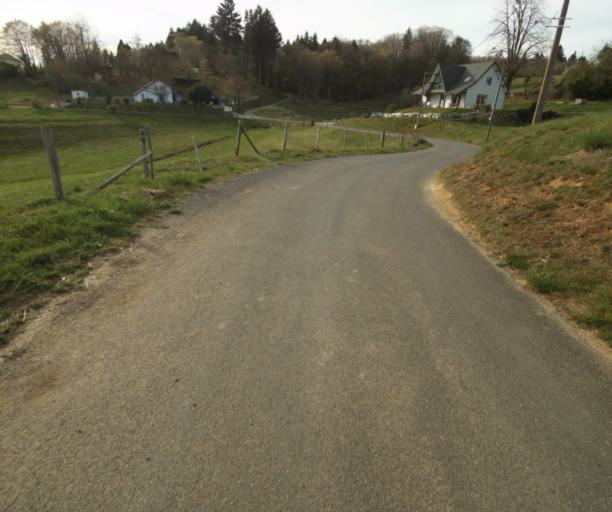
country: FR
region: Limousin
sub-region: Departement de la Correze
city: Naves
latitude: 45.3229
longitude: 1.7581
